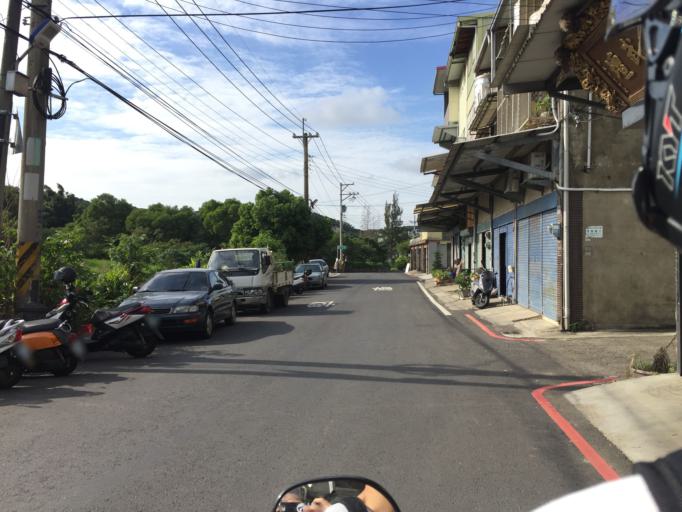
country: TW
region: Taiwan
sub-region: Hsinchu
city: Hsinchu
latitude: 24.7729
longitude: 120.9341
